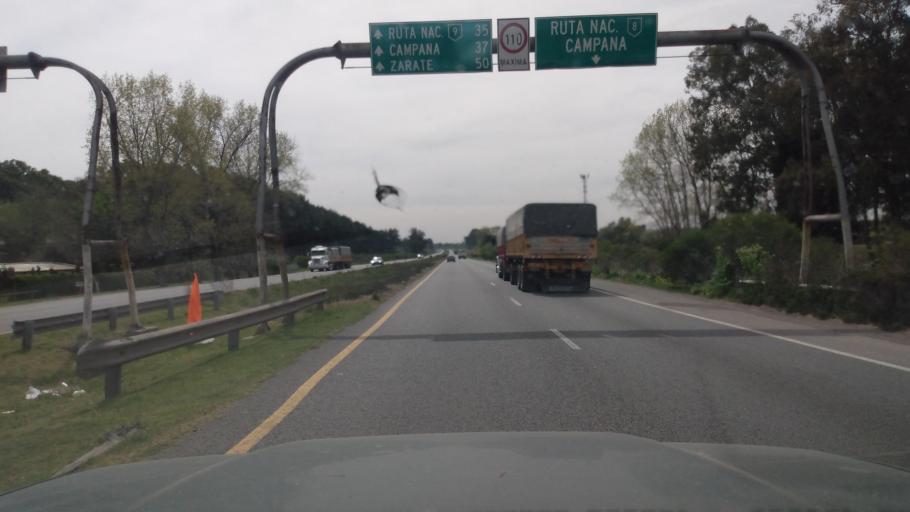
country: AR
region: Buenos Aires
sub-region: Partido de Lujan
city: Lujan
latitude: -34.4650
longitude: -59.0638
